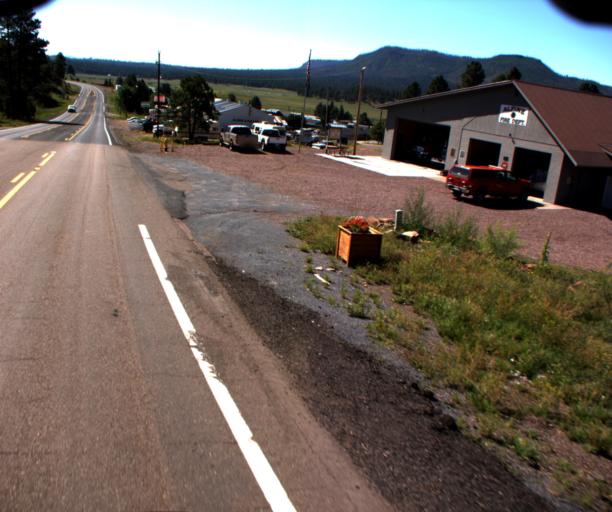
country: US
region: Arizona
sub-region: Apache County
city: Eagar
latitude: 33.8474
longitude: -109.1391
